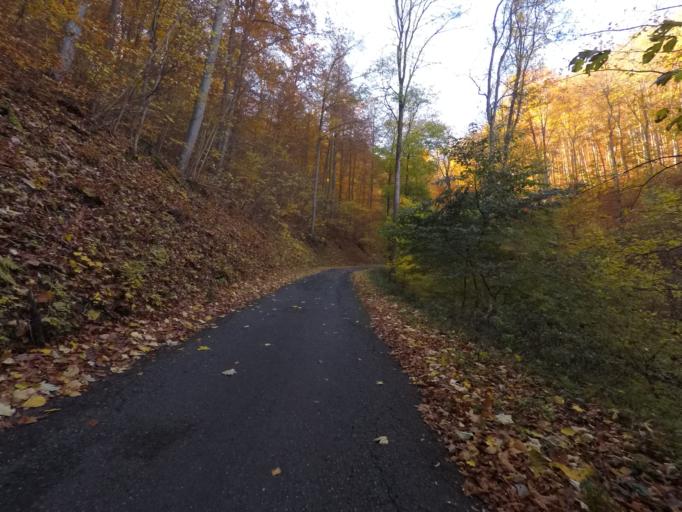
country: DE
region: Baden-Wuerttemberg
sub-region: Tuebingen Region
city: Pfullingen
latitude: 48.4362
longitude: 9.2332
